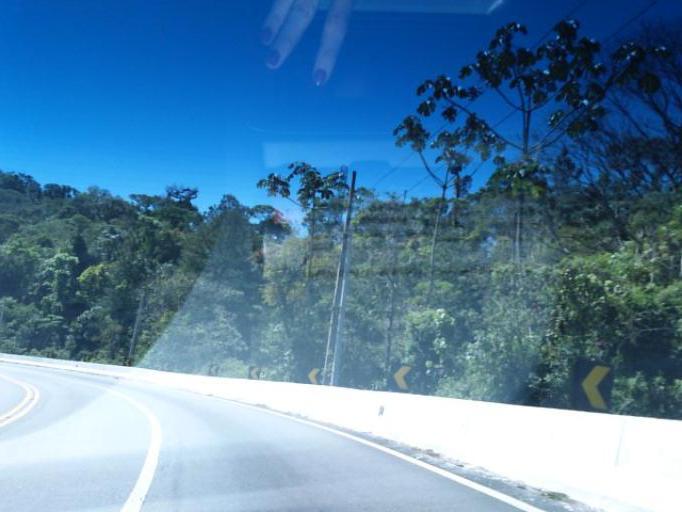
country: BR
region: Sao Paulo
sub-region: Campos Do Jordao
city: Campos do Jordao
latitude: -22.8233
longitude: -45.6225
